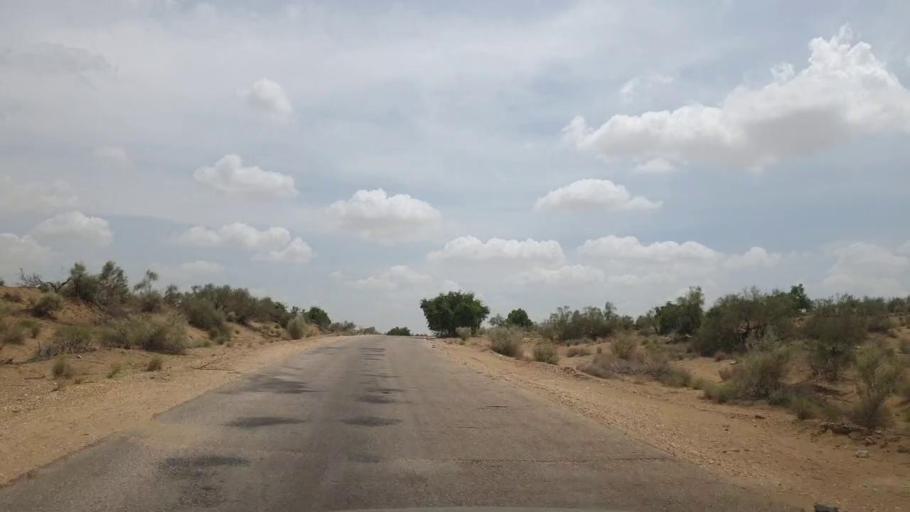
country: PK
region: Sindh
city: Kot Diji
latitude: 27.1602
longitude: 69.2233
